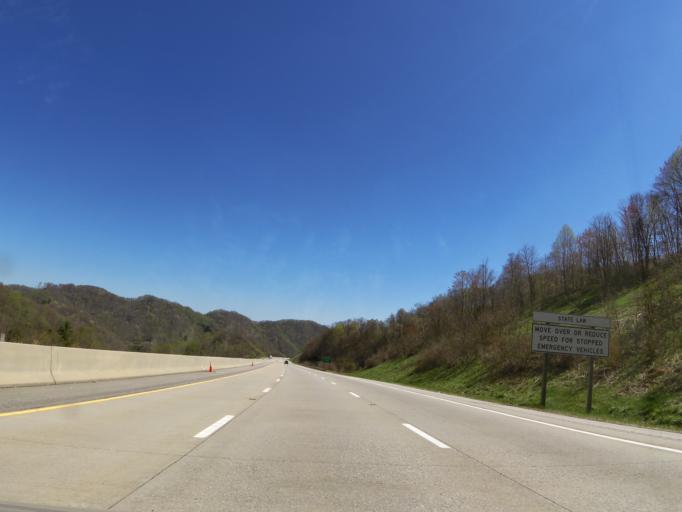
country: US
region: North Carolina
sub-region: Madison County
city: Mars Hill
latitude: 35.9428
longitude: -82.5640
